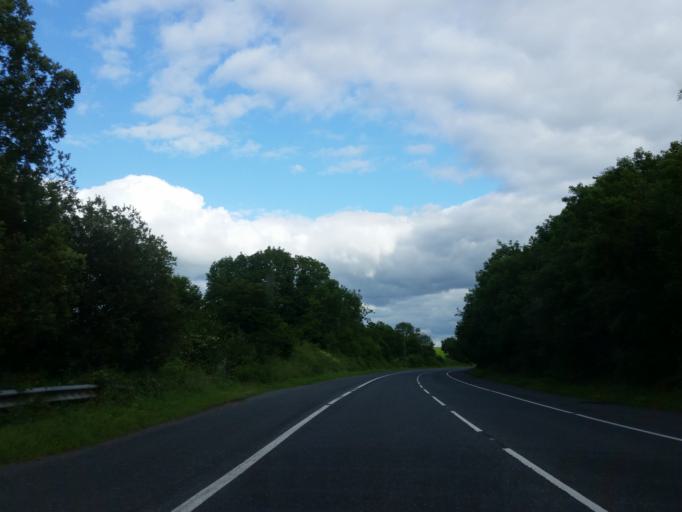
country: GB
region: Northern Ireland
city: Lisnaskea
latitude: 54.3122
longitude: -7.5011
